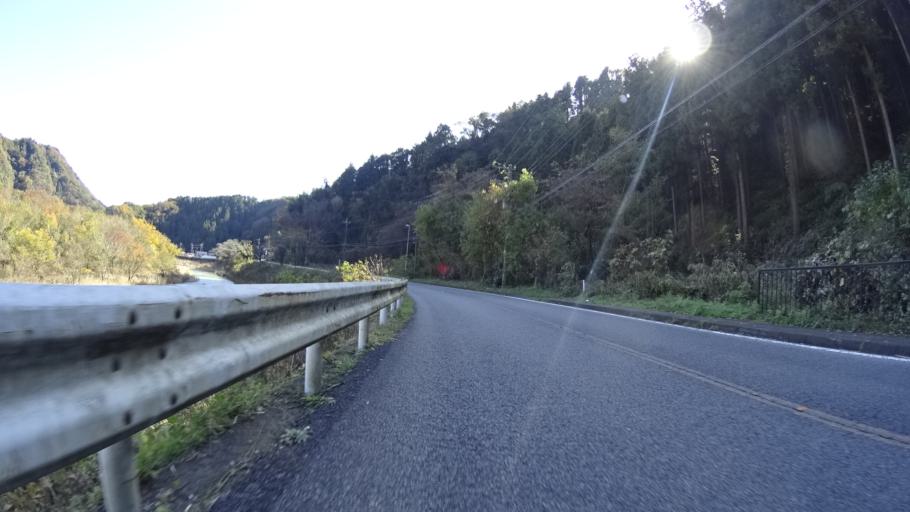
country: JP
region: Kanagawa
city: Zama
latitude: 35.5374
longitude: 139.2777
